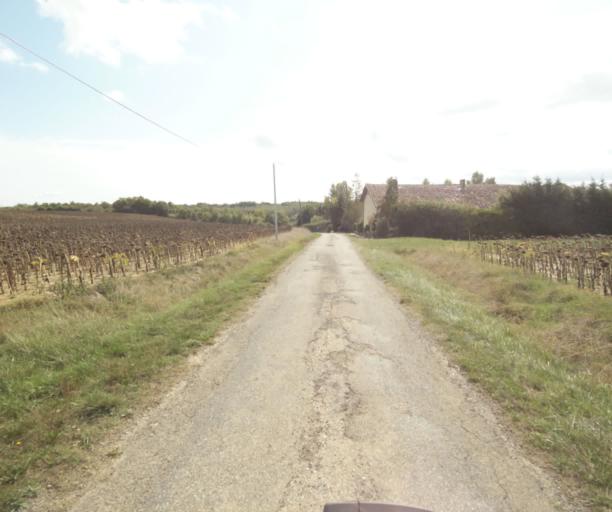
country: FR
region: Midi-Pyrenees
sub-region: Departement du Tarn-et-Garonne
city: Verdun-sur-Garonne
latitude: 43.8593
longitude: 1.1775
